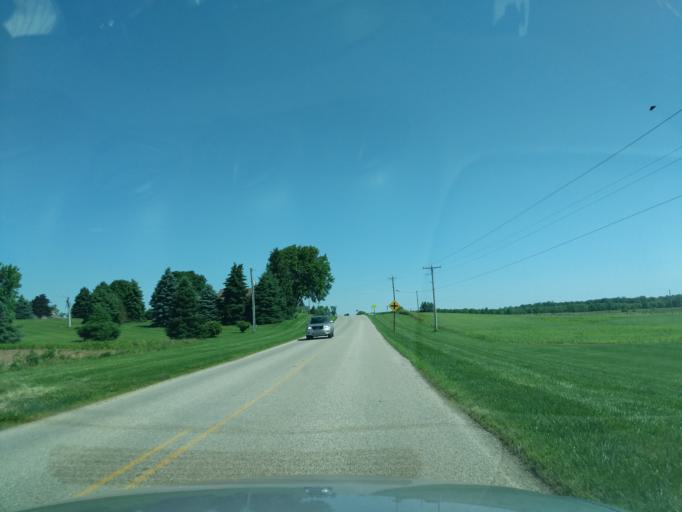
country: US
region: Indiana
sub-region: Huntington County
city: Huntington
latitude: 40.8275
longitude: -85.5084
